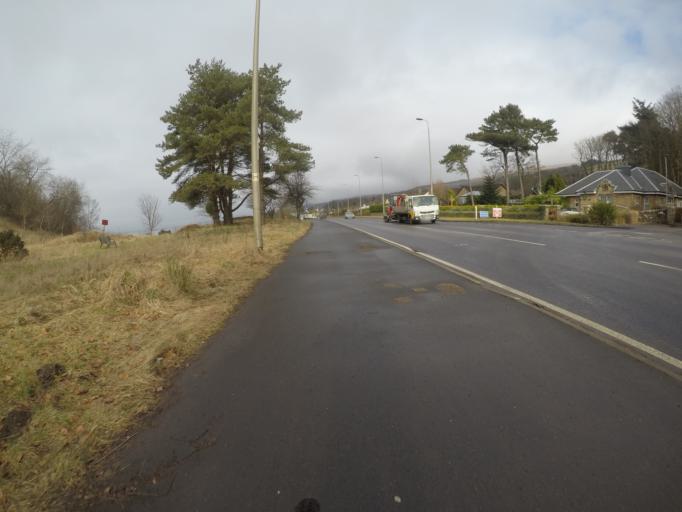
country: GB
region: Scotland
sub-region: North Ayrshire
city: Fairlie
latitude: 55.7465
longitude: -4.8573
